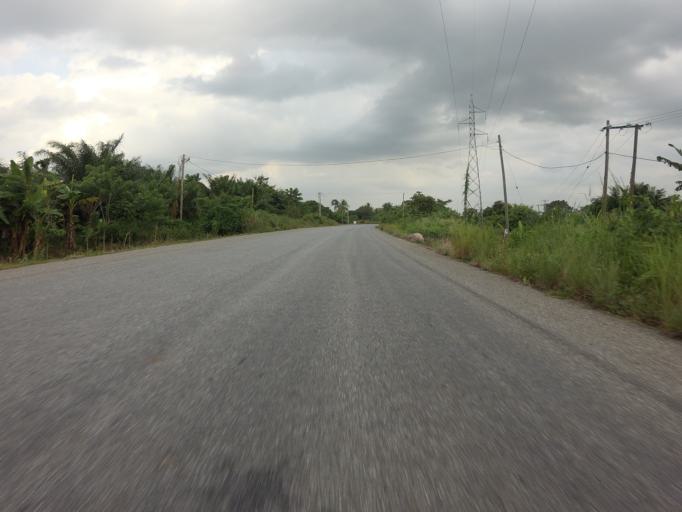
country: GH
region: Volta
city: Ho
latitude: 6.4818
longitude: 0.4945
